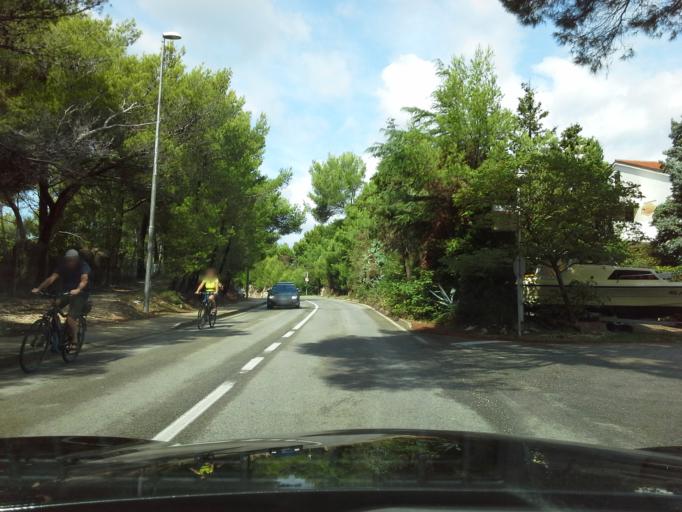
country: HR
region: Primorsko-Goranska
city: Mali Losinj
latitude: 44.5441
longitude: 14.4630
